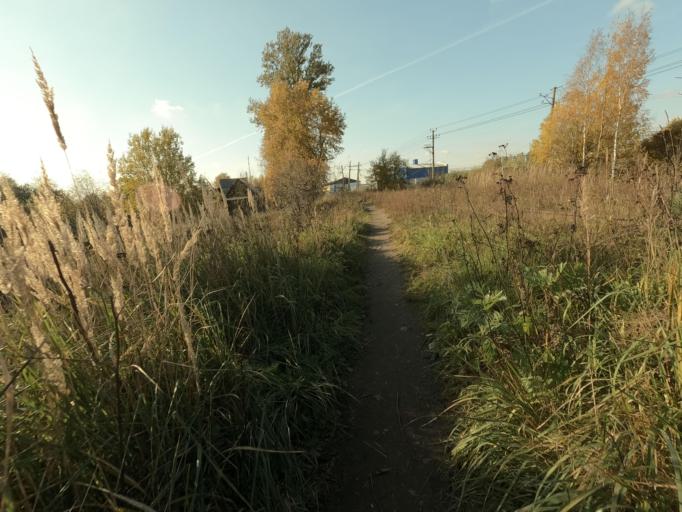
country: RU
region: Leningrad
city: Mga
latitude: 59.7536
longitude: 31.0653
